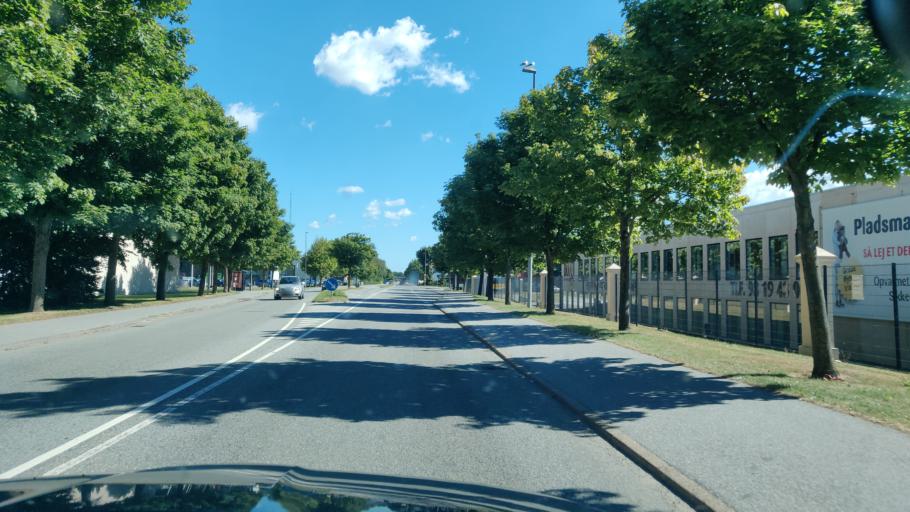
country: DK
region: North Denmark
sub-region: Alborg Kommune
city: Vestbjerg
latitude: 57.0806
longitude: 9.9583
